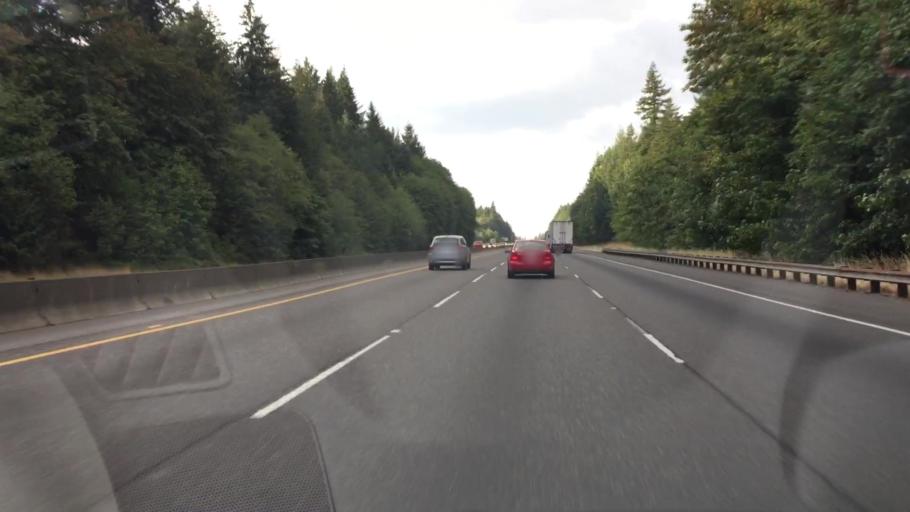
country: US
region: Washington
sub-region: Cowlitz County
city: Castle Rock
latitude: 46.3373
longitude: -122.9077
